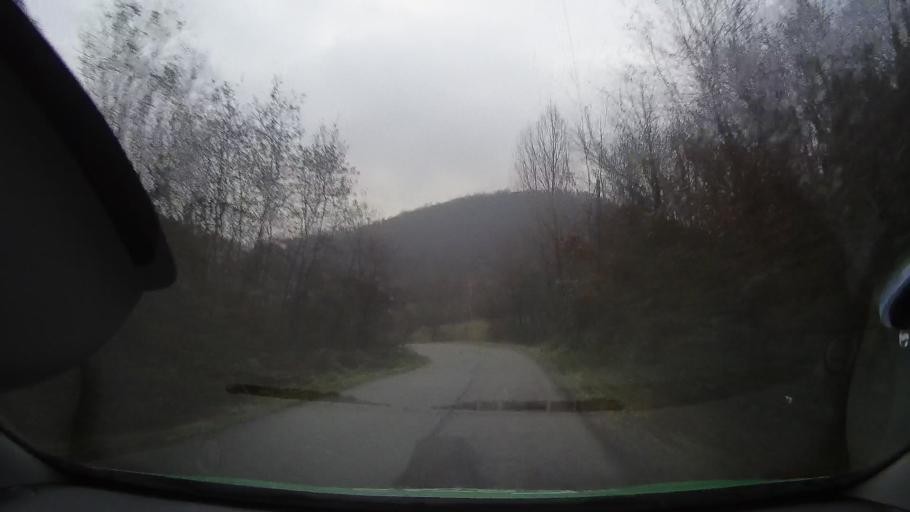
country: RO
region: Hunedoara
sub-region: Comuna Ribita
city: Ribita
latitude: 46.2326
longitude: 22.7465
